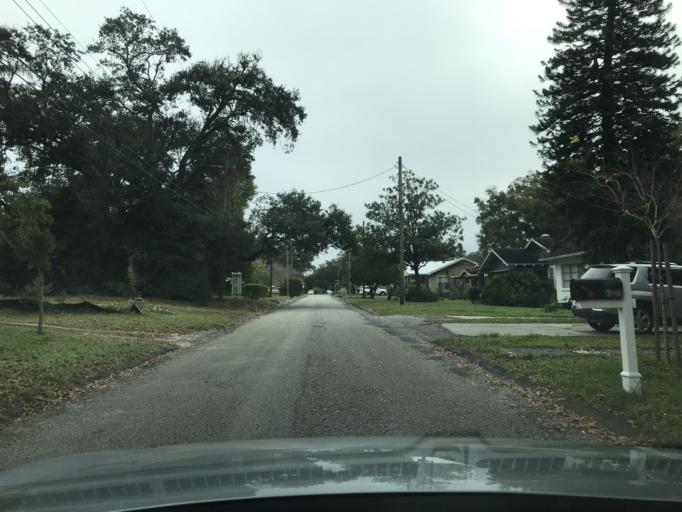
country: US
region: Florida
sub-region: Hillsborough County
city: Tampa
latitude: 27.9914
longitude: -82.4636
